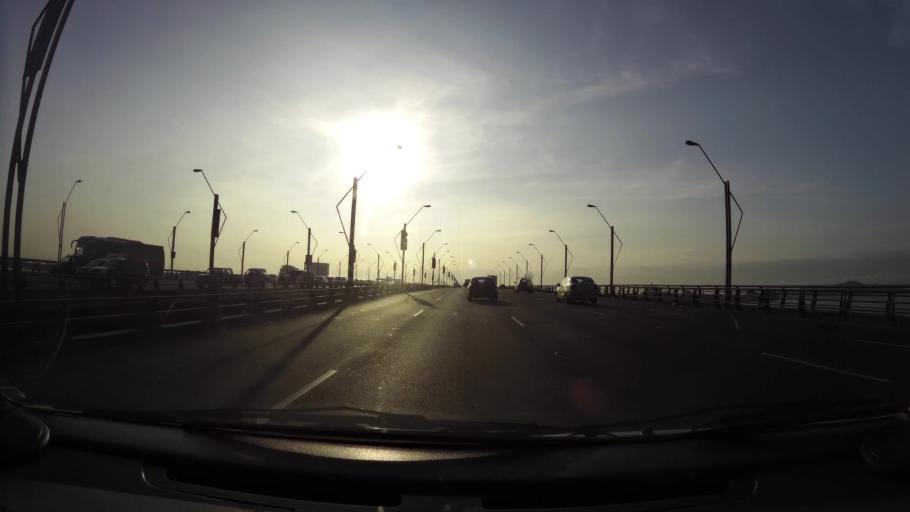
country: EC
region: Guayas
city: Eloy Alfaro
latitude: -2.1542
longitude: -79.8752
